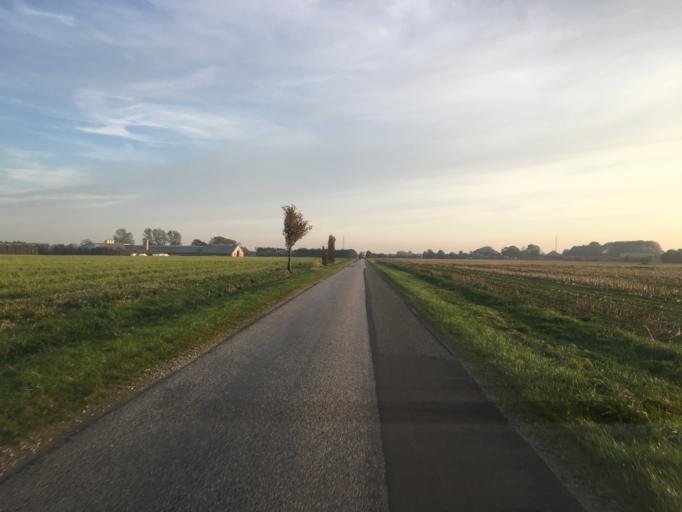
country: DK
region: South Denmark
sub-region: Tonder Kommune
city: Logumkloster
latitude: 55.0458
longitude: 9.0258
